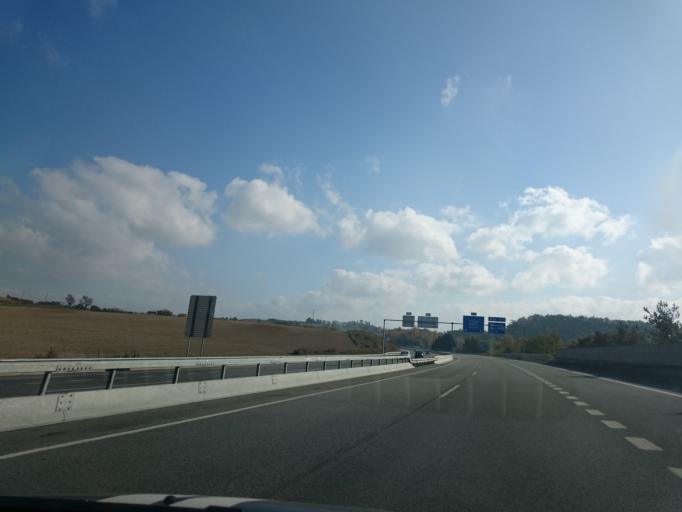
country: ES
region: Catalonia
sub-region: Provincia de Barcelona
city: Gurb
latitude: 41.9328
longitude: 2.2034
